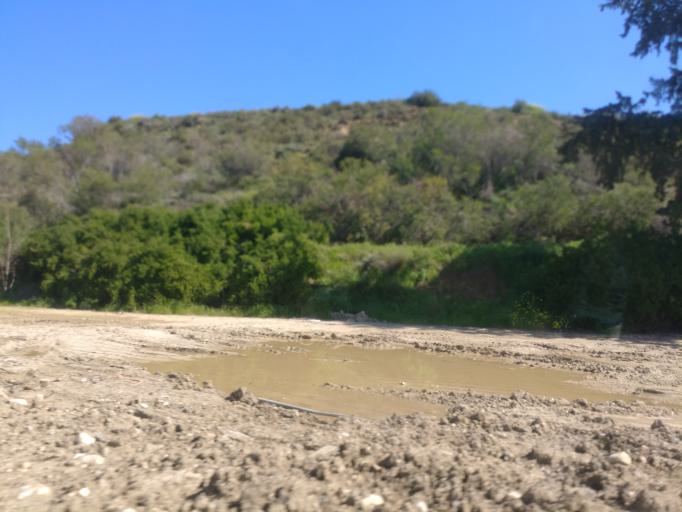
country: CY
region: Pafos
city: Polis
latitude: 35.0091
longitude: 32.4372
